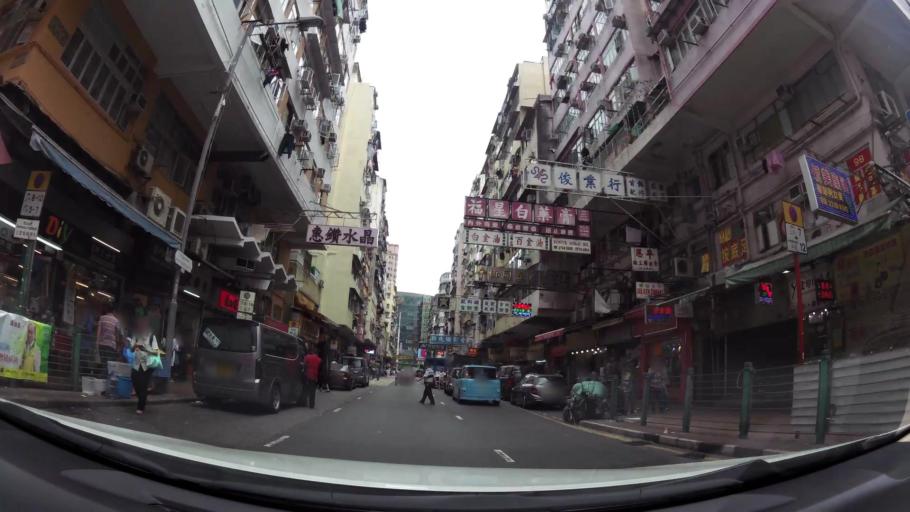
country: HK
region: Sham Shui Po
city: Sham Shui Po
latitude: 22.3295
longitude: 114.1619
